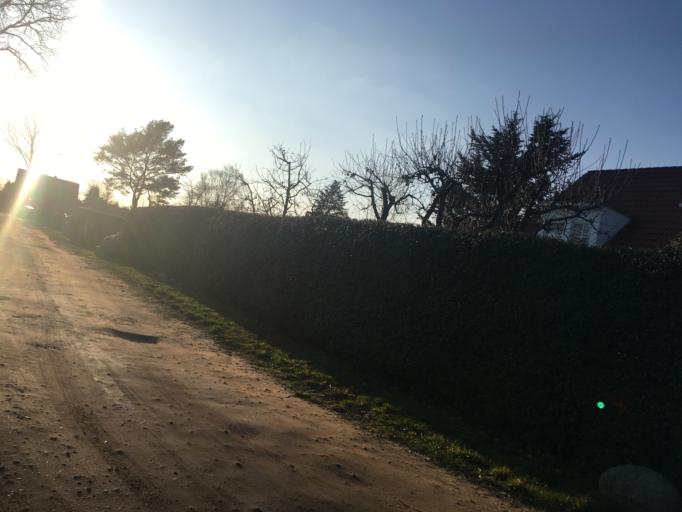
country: DE
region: Berlin
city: Karow
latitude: 52.6051
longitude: 13.4848
